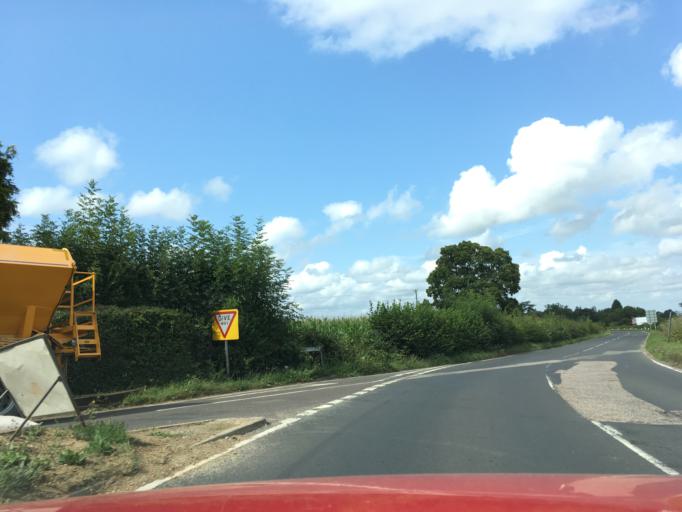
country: GB
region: England
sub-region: Kent
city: Tenterden
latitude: 51.1057
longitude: 0.6441
